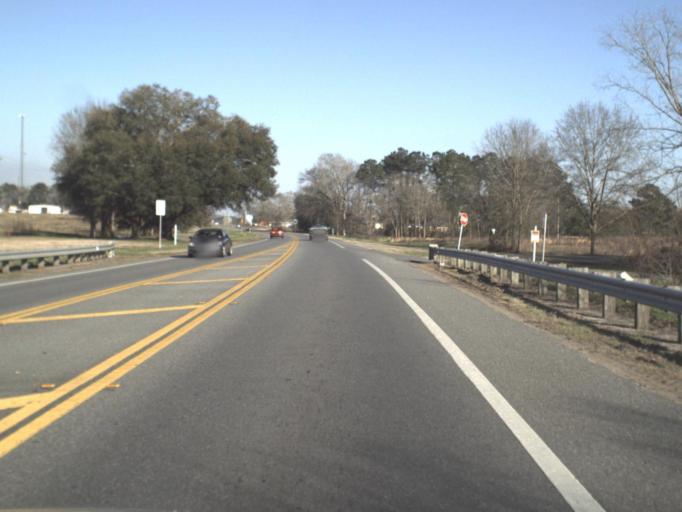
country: US
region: Florida
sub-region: Jackson County
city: Sneads
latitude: 30.7087
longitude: -84.9099
